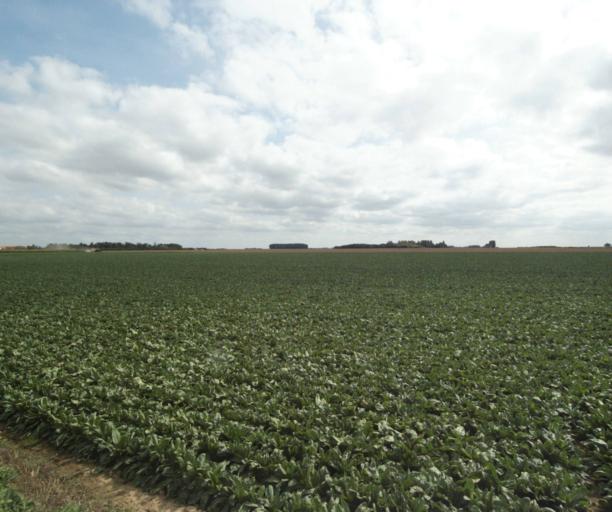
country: FR
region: Nord-Pas-de-Calais
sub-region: Departement du Nord
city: Baisieux
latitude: 50.6024
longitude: 3.2317
